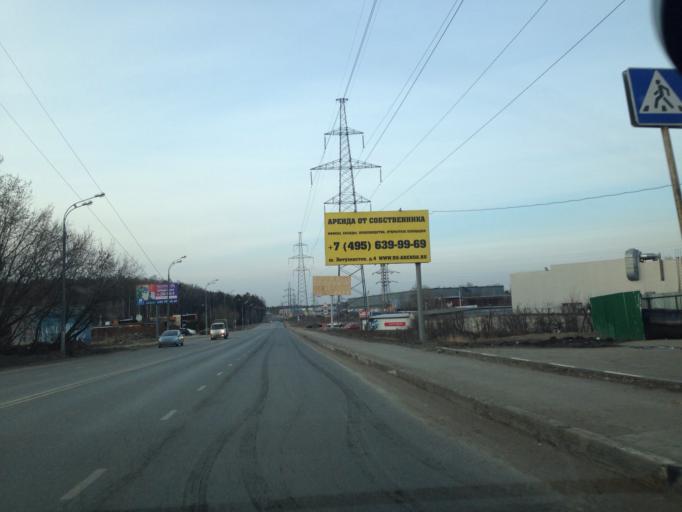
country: RU
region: Moscow
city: Vostochnyy
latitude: 55.7914
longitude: 37.8950
